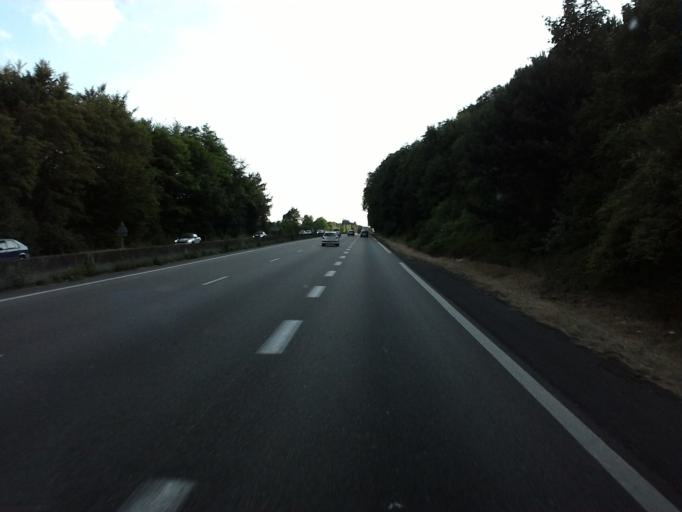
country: FR
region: Lorraine
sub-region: Departement de Meurthe-et-Moselle
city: Maxeville
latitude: 48.7097
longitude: 6.1442
